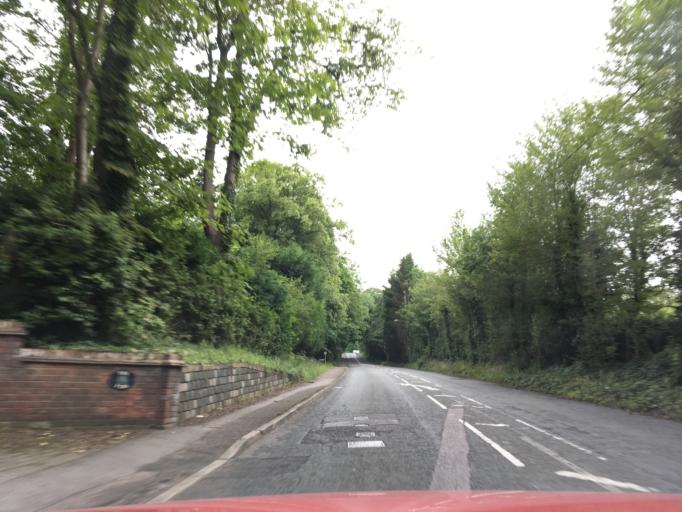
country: GB
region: England
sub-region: Oxfordshire
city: Oxford
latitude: 51.7248
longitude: -1.2649
